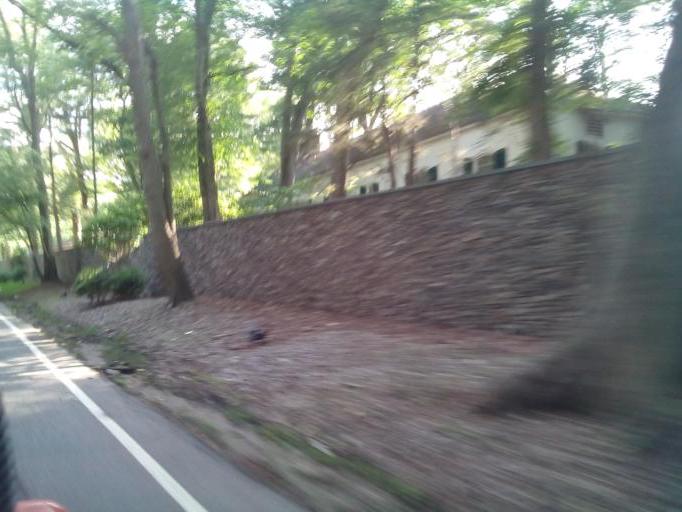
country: US
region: New York
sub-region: Nassau County
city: Upper Brookville
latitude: 40.8563
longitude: -73.5693
